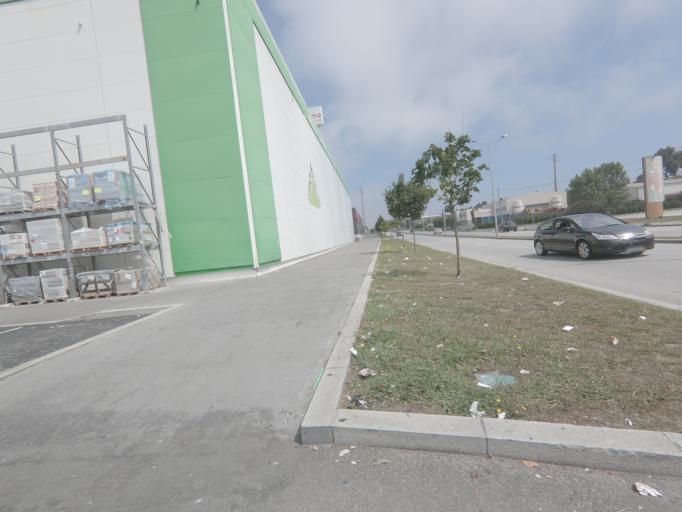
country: PT
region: Porto
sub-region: Matosinhos
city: Santa Cruz do Bispo
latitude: 41.2114
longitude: -8.6835
